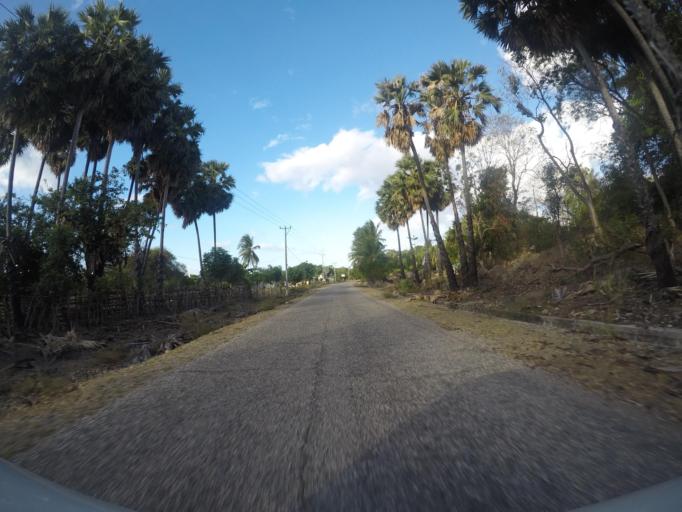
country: TL
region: Lautem
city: Lospalos
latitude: -8.3388
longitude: 126.9365
